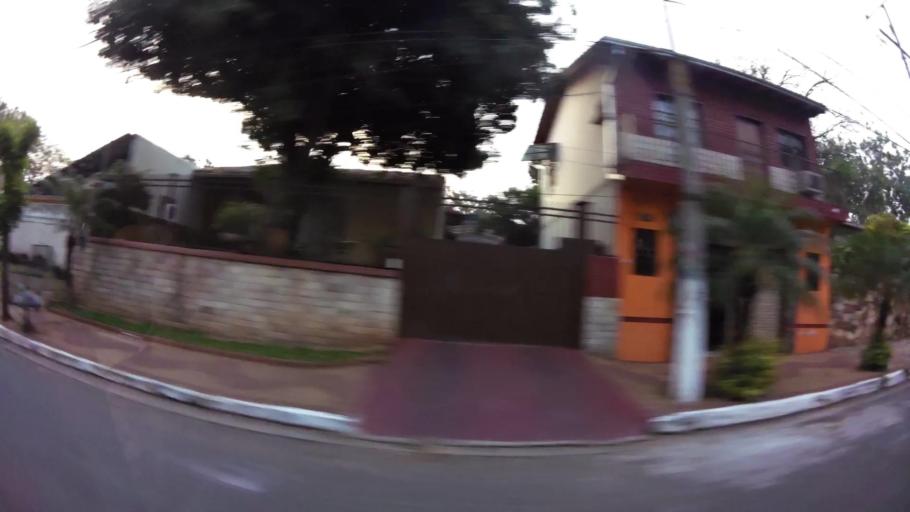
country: PY
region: Central
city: Lambare
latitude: -25.3382
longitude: -57.6228
